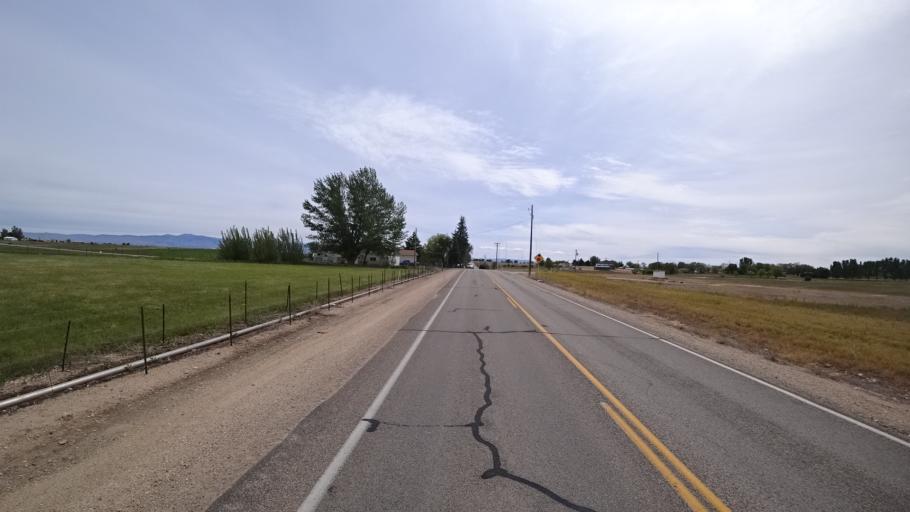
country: US
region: Idaho
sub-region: Ada County
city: Meridian
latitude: 43.5611
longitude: -116.4168
